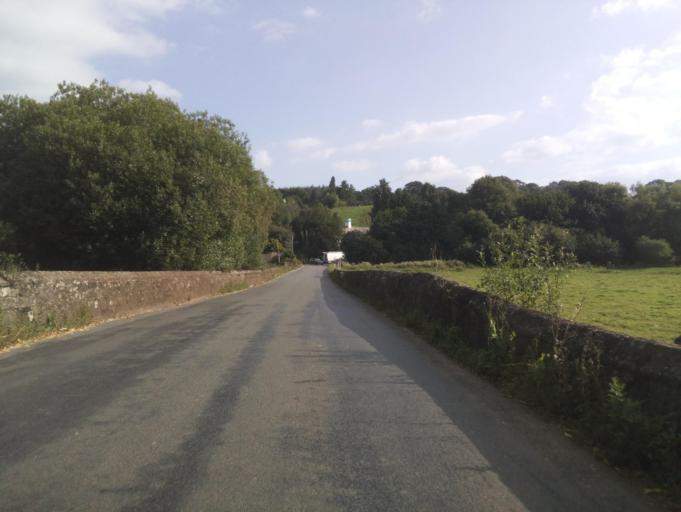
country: GB
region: England
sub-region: Devon
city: Heavitree
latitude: 50.7670
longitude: -3.5068
